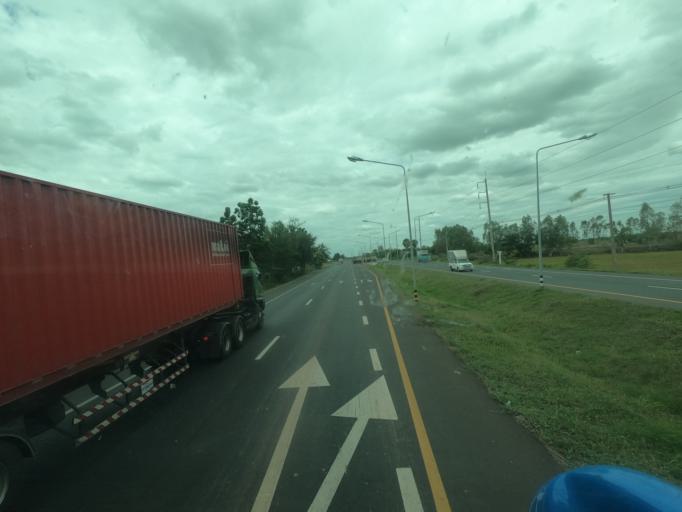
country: TH
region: Buriram
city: Prakhon Chai
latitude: 14.6105
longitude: 103.0538
